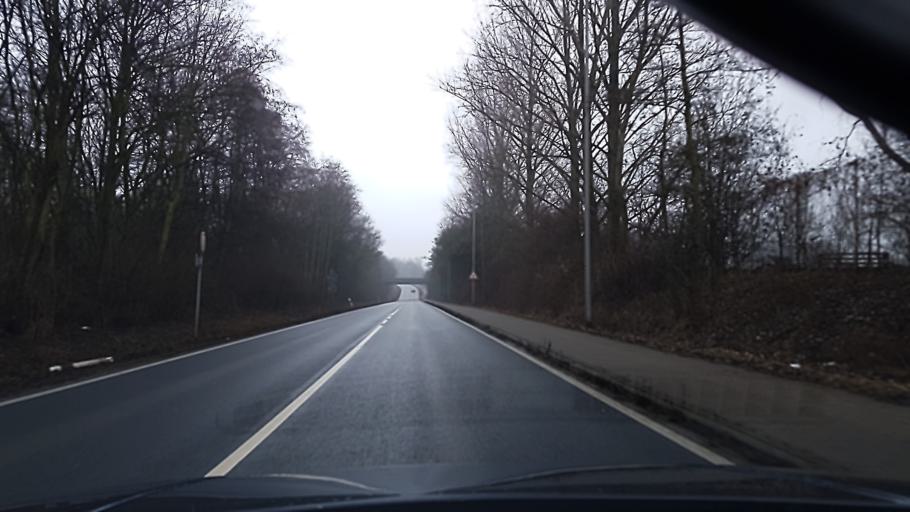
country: DE
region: Lower Saxony
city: Cramme
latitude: 52.1547
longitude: 10.4217
